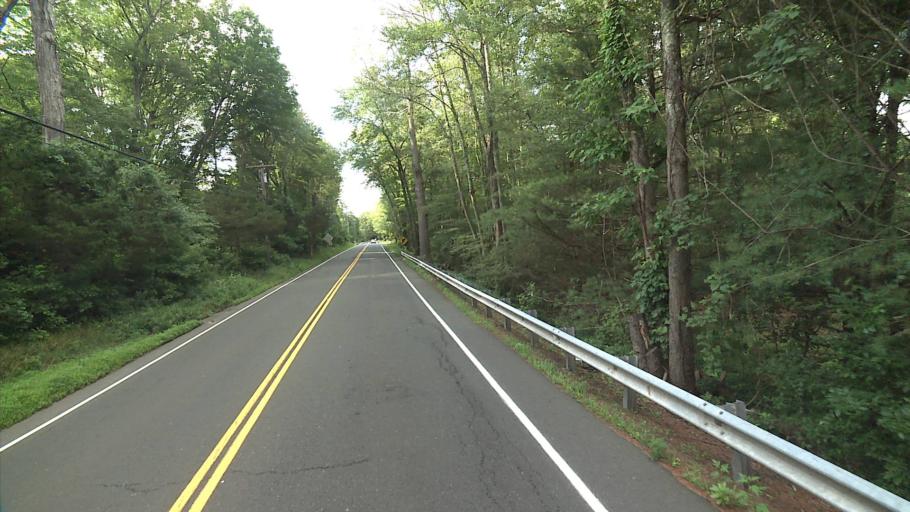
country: US
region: Connecticut
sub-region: Middlesex County
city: Higganum
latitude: 41.4034
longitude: -72.5622
